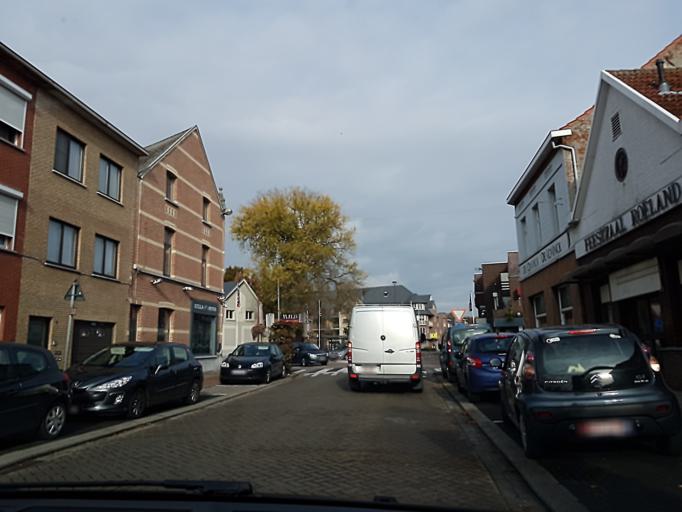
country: BE
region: Flanders
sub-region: Provincie Antwerpen
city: Lint
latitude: 51.1269
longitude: 4.4968
